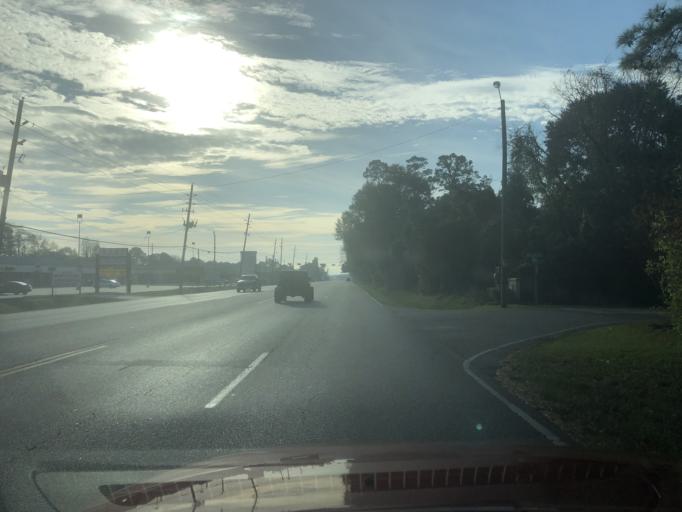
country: US
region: Texas
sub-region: Harris County
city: Spring
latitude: 30.0158
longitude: -95.4703
